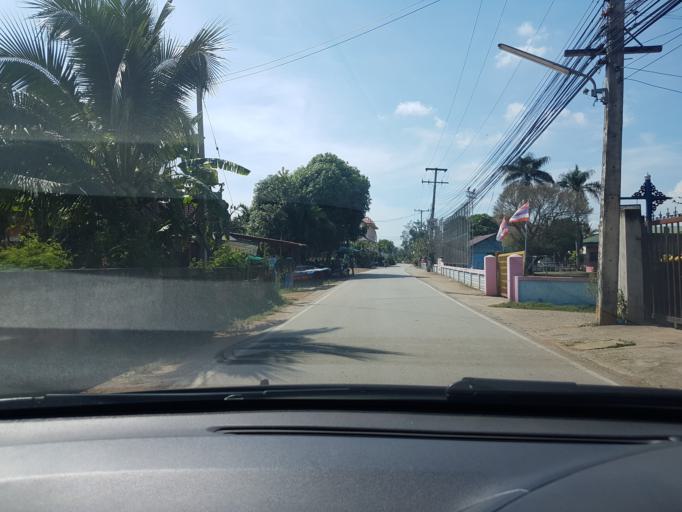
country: TH
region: Lampang
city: Ko Kha
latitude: 18.2173
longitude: 99.4127
